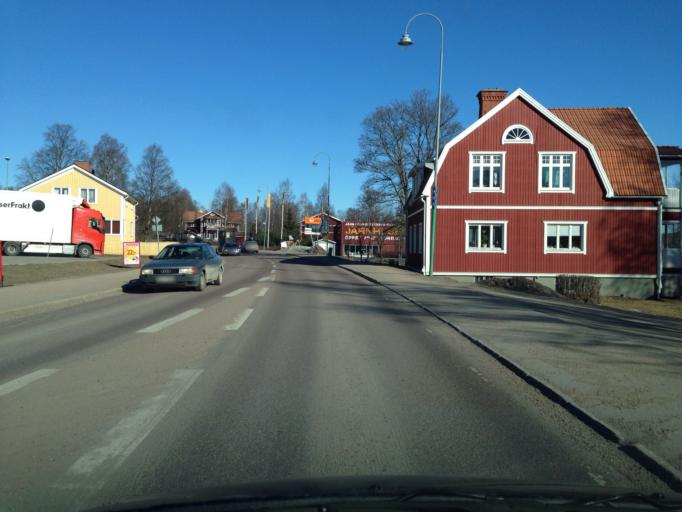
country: SE
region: Gaevleborg
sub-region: Ljusdals Kommun
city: Jaervsoe
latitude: 61.7176
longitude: 16.1702
